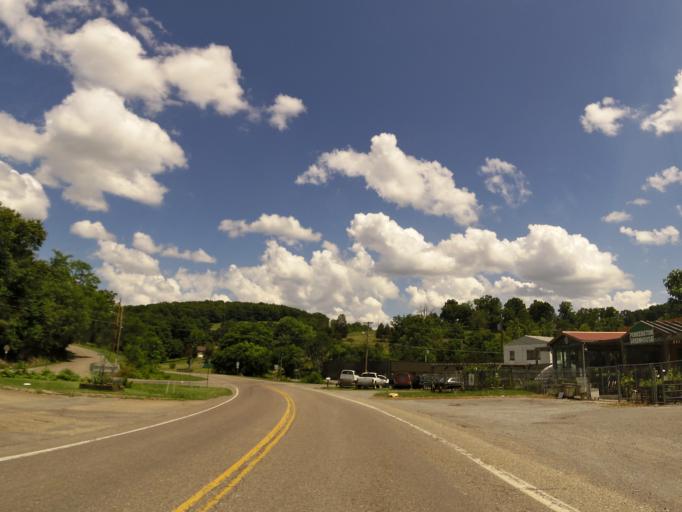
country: US
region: Virginia
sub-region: Lee County
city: Jonesville
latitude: 36.6878
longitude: -83.1051
